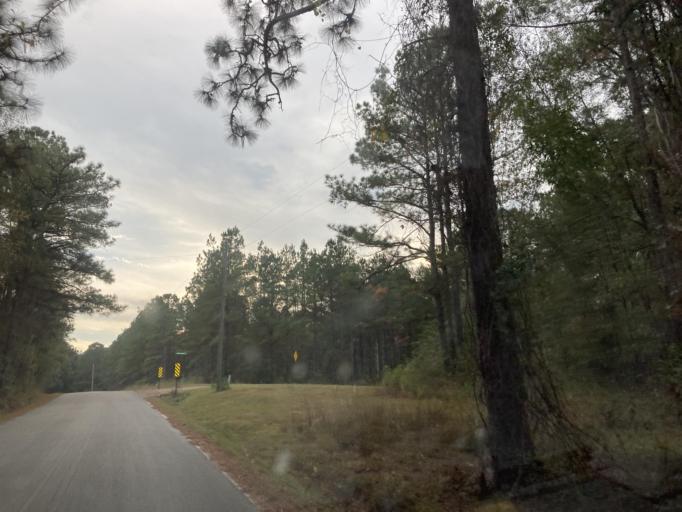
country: US
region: Mississippi
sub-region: Lamar County
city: Purvis
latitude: 31.1771
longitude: -89.3883
